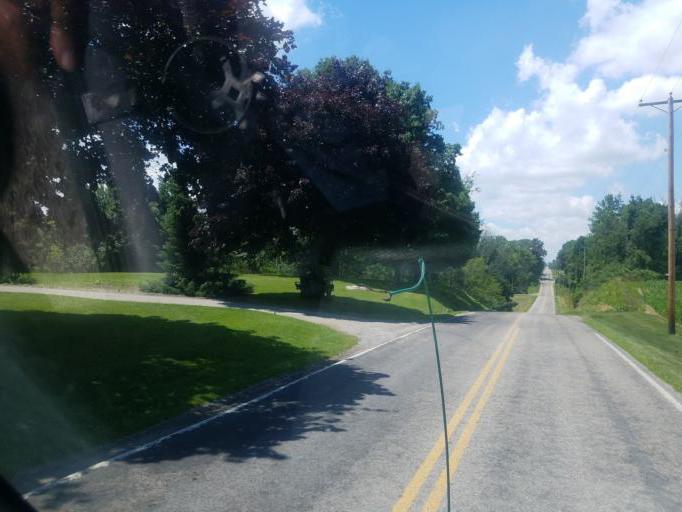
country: US
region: Ohio
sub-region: Huron County
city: Plymouth
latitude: 41.0682
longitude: -82.6496
